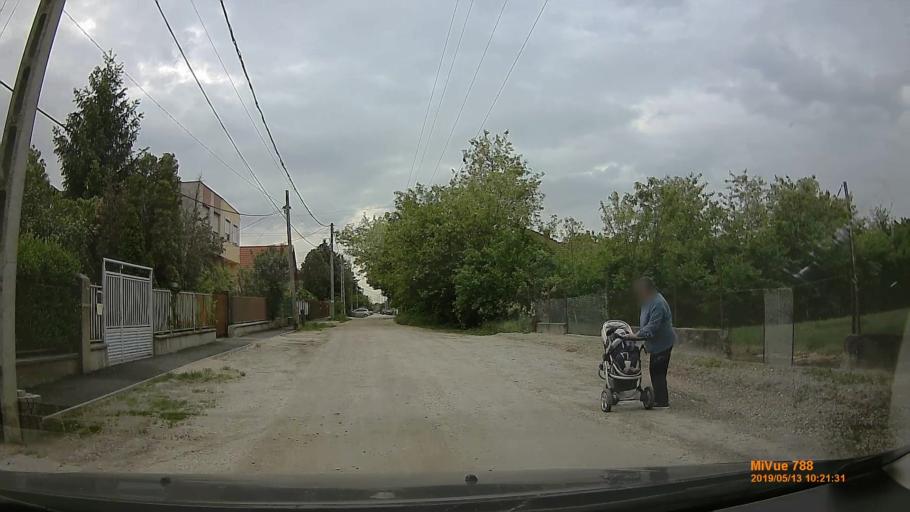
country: HU
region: Budapest
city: Budapest XXIII. keruelet
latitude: 47.3957
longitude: 19.0902
